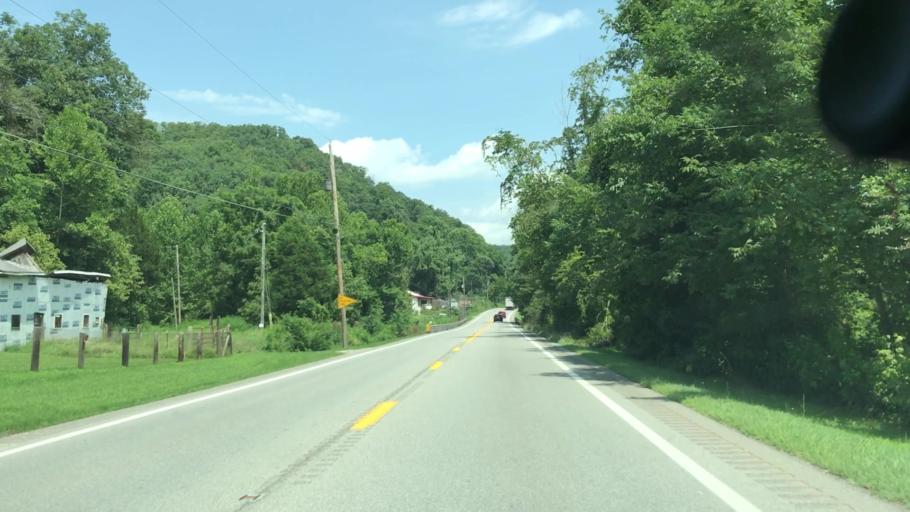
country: US
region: West Virginia
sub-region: Putnam County
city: Buffalo
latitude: 38.6010
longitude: -82.0042
